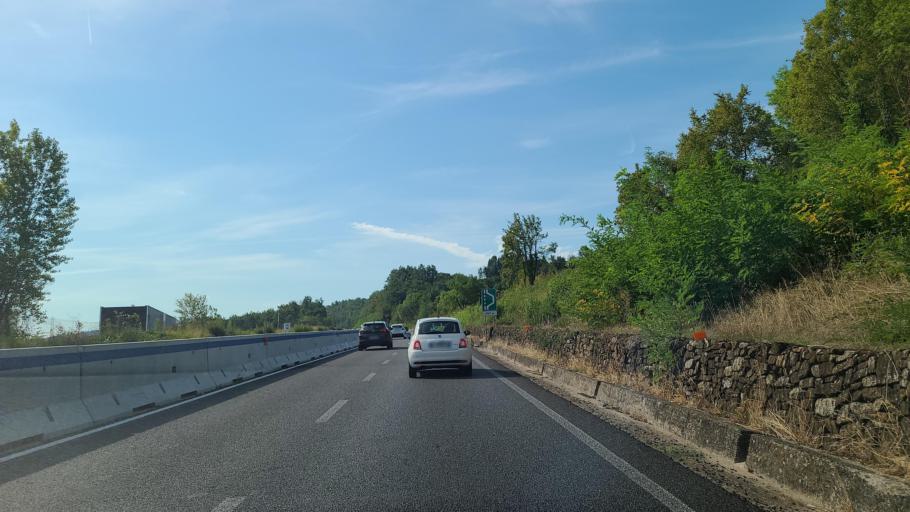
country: IT
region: Tuscany
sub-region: Province of Florence
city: Sambuca
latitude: 43.5786
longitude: 11.2040
